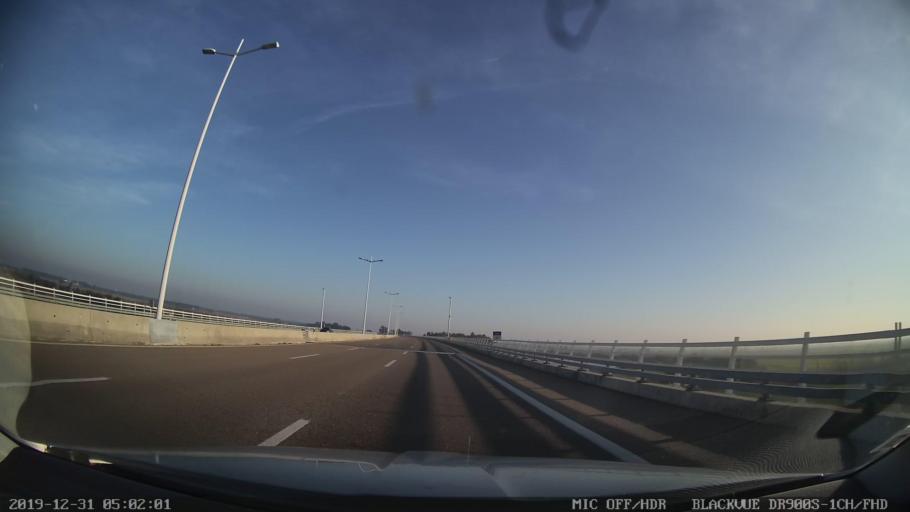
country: PT
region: Santarem
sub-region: Benavente
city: Samora Correia
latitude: 38.9753
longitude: -8.8808
